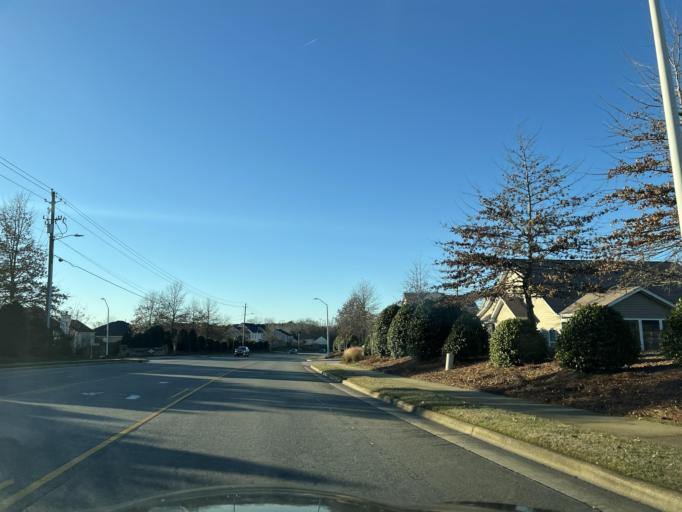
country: US
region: North Carolina
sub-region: Wake County
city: Fuquay-Varina
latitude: 35.5742
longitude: -78.8069
